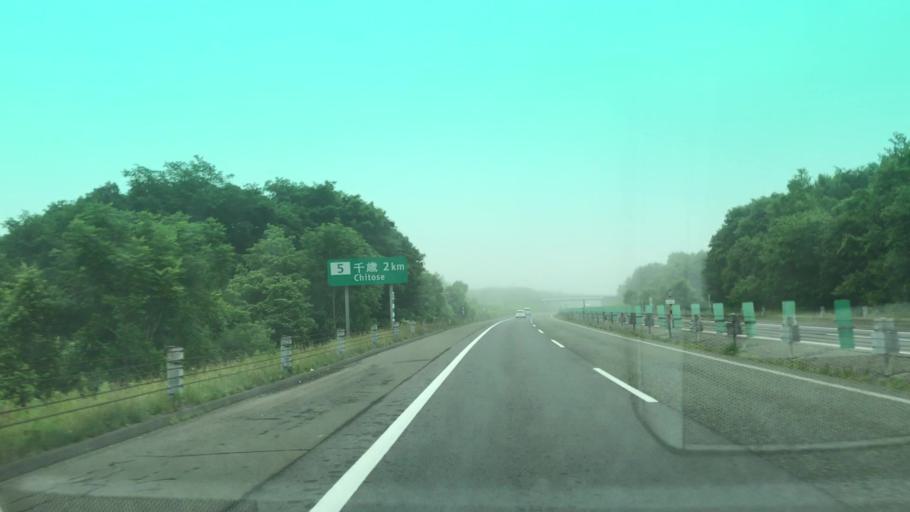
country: JP
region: Hokkaido
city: Chitose
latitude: 42.8303
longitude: 141.6123
